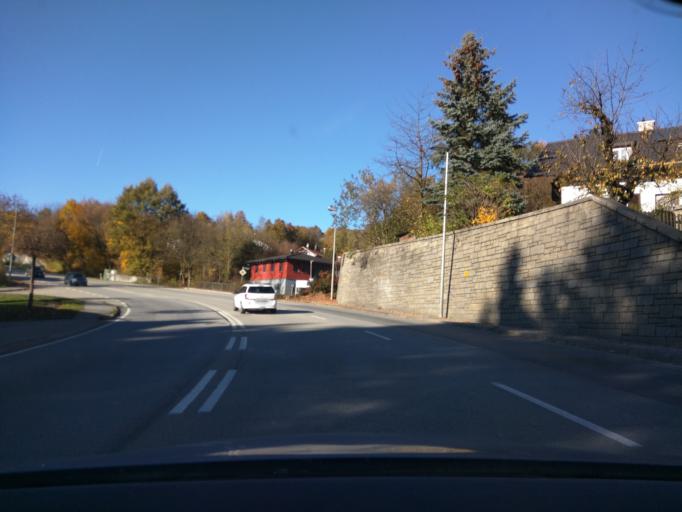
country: DE
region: Bavaria
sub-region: Lower Bavaria
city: Salzweg
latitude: 48.5835
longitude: 13.4765
